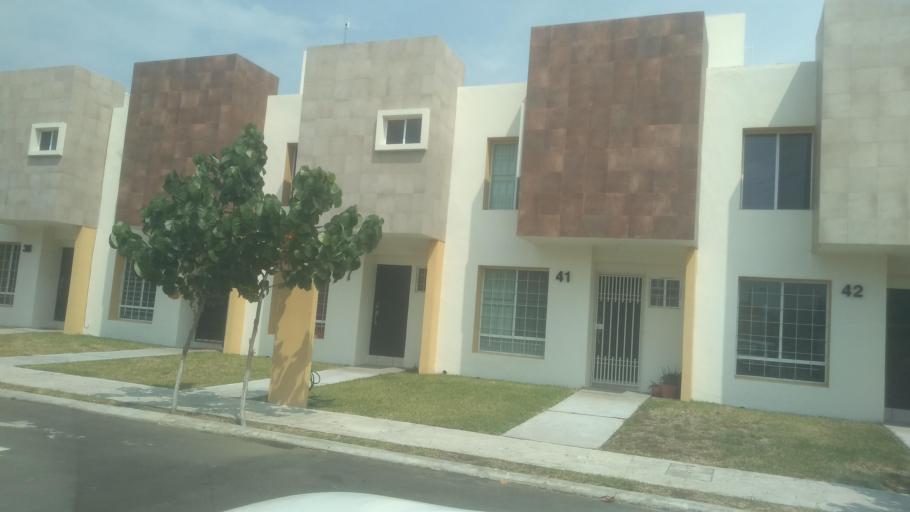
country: MX
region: Veracruz
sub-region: Veracruz
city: Las Amapolas
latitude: 19.1671
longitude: -96.1804
